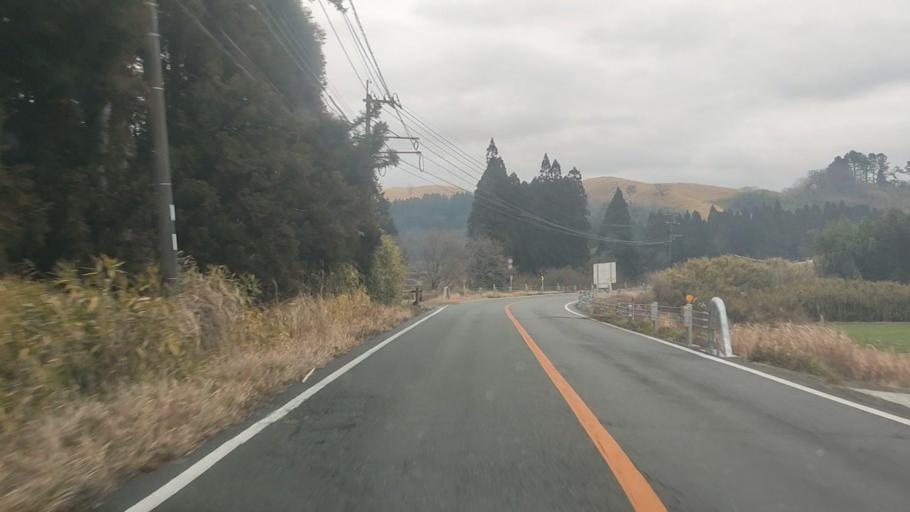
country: JP
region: Kumamoto
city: Aso
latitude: 32.9008
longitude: 130.9980
